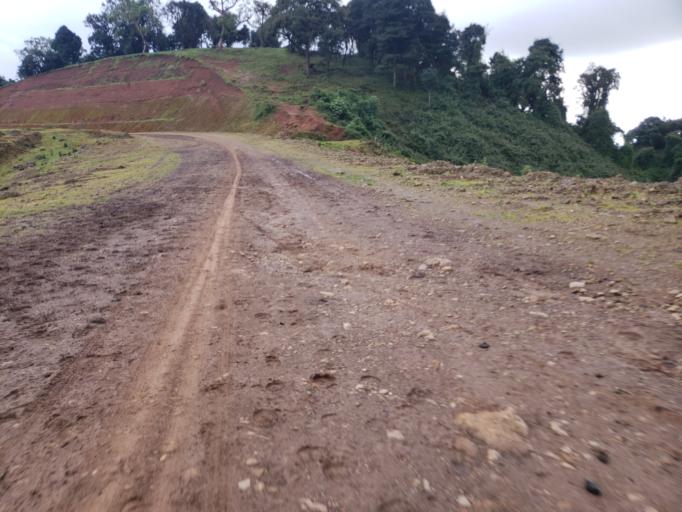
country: ET
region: Oromiya
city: Dodola
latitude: 6.6716
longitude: 39.3643
